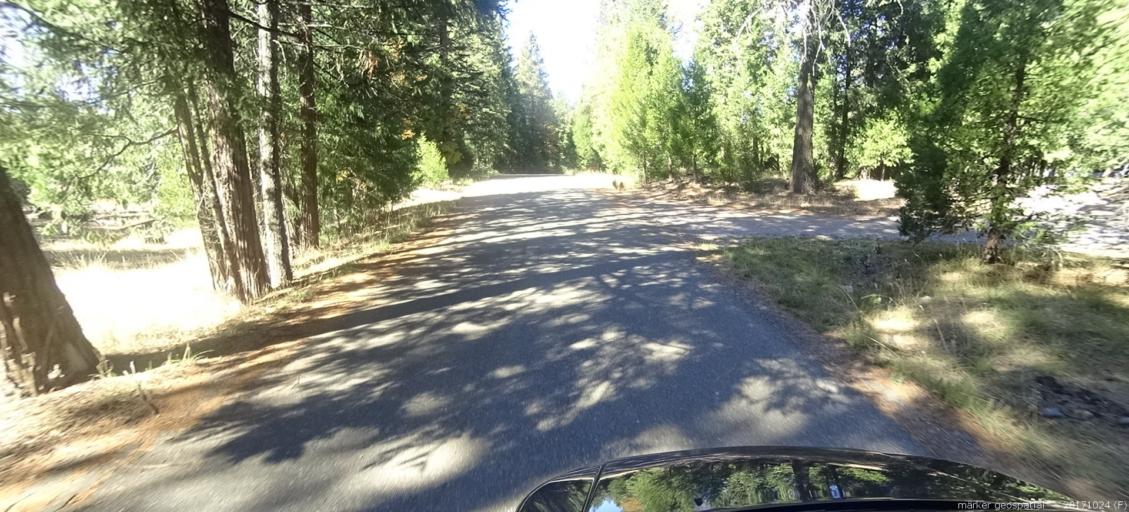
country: US
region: California
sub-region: Shasta County
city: Shingletown
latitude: 40.5164
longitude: -121.6810
